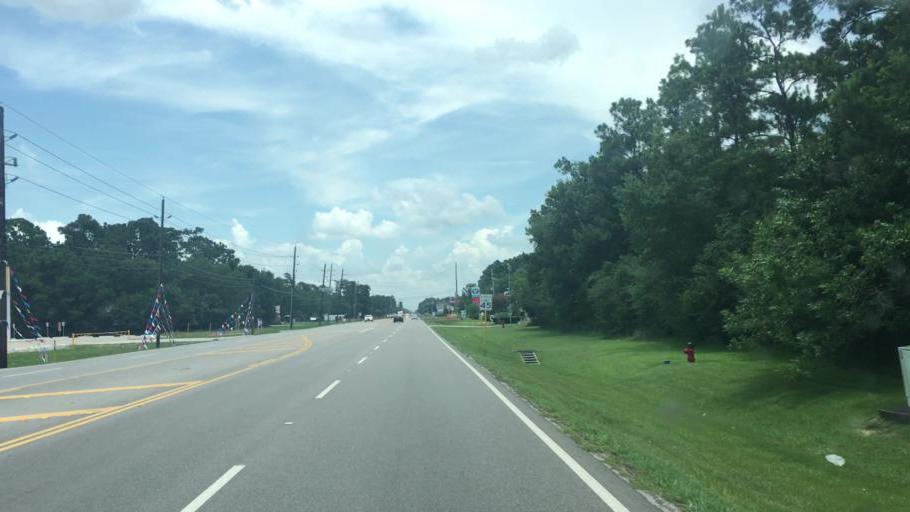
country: US
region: Texas
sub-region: Harris County
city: Atascocita
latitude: 29.9858
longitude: -95.2005
